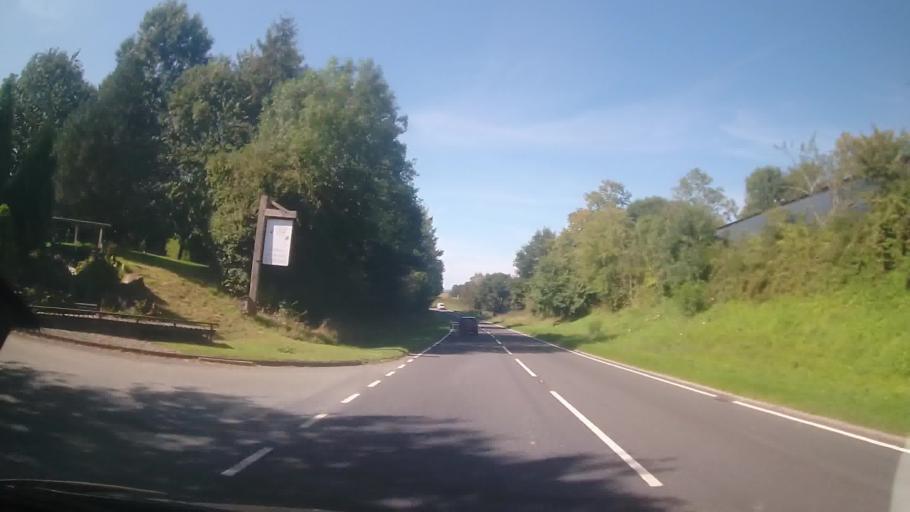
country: GB
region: England
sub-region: Shropshire
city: Bishop's Castle
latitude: 52.5289
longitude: -3.0295
